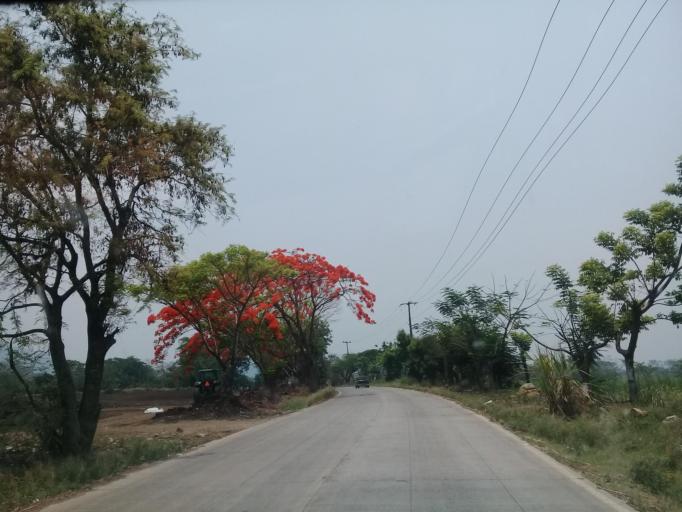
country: MX
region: Veracruz
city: Cosolapa
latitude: 18.5865
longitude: -96.7001
